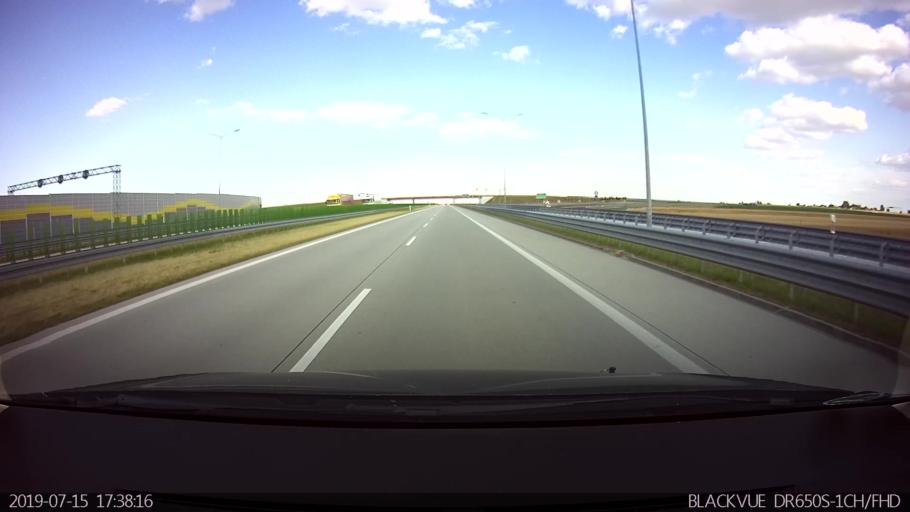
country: PL
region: Lodz Voivodeship
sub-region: Powiat wieruszowski
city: Walichnowy
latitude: 51.3162
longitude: 18.3811
